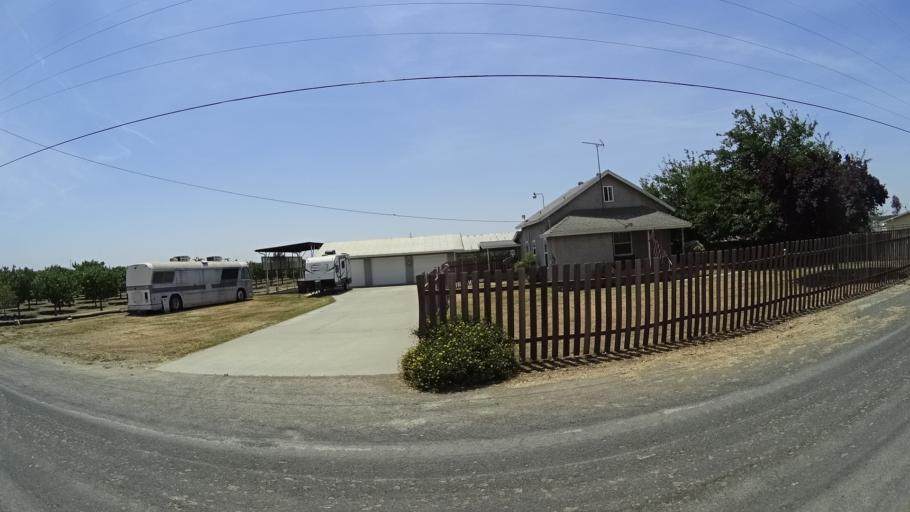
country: US
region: California
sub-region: Fresno County
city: Riverdale
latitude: 36.3948
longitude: -119.8270
